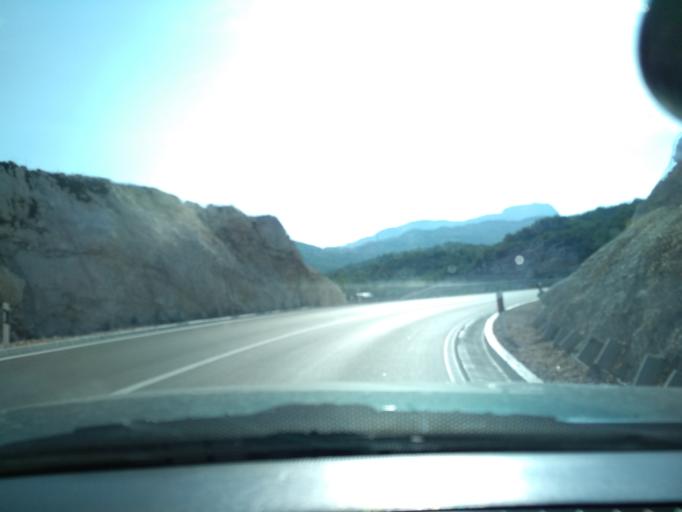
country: ME
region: Cetinje
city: Cetinje
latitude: 42.4047
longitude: 18.8904
